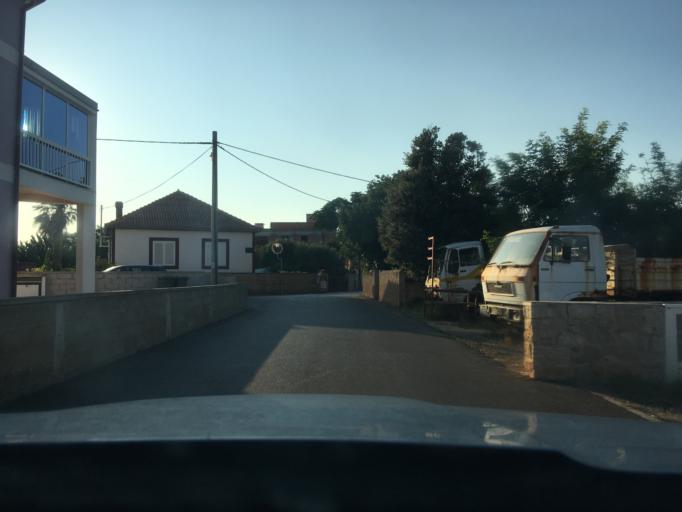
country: HR
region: Zadarska
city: Vir
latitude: 44.3049
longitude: 15.0787
